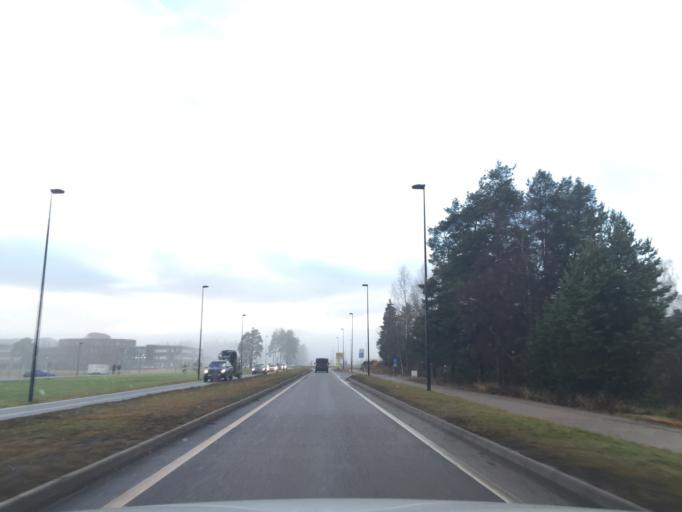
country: NO
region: Hedmark
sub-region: Elverum
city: Elverum
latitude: 60.8817
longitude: 11.5441
